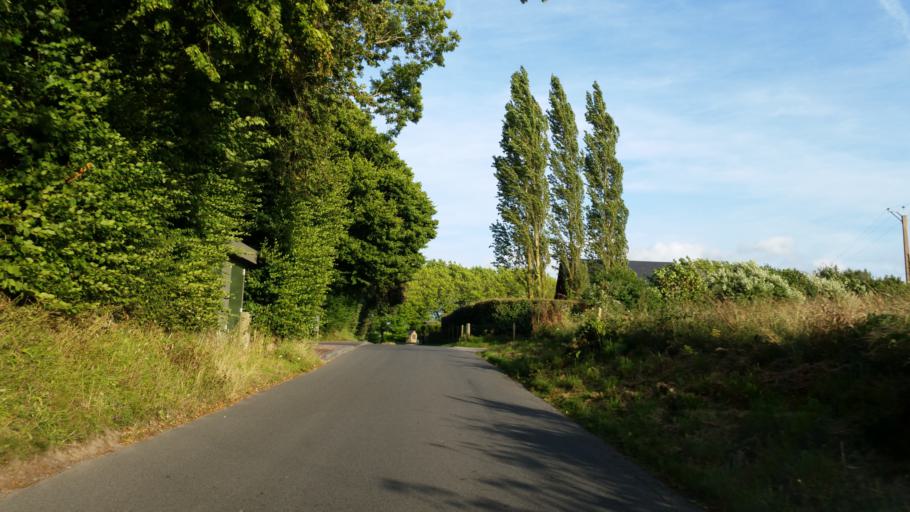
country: FR
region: Lower Normandy
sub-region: Departement du Calvados
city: La Riviere-Saint-Sauveur
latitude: 49.3788
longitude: 0.2474
